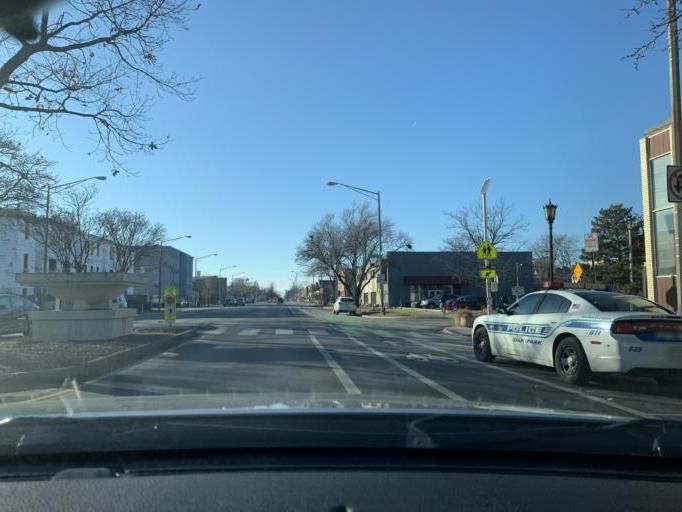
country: US
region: Illinois
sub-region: Cook County
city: Oak Park
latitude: 41.8801
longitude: -87.7760
